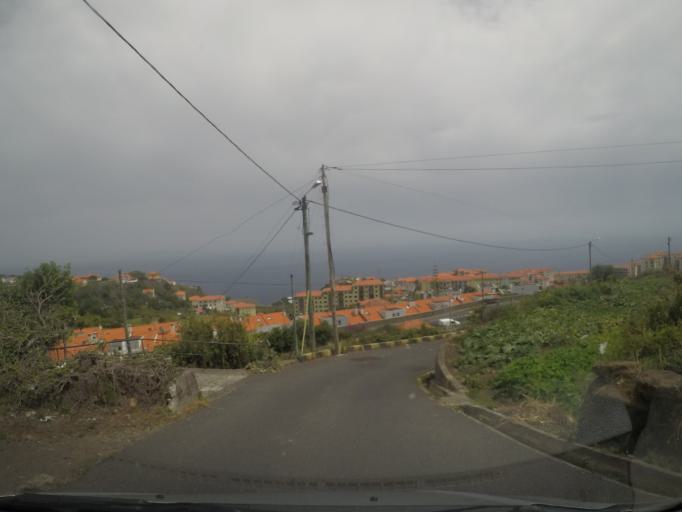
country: PT
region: Madeira
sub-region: Santa Cruz
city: Camacha
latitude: 32.6589
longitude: -16.8293
